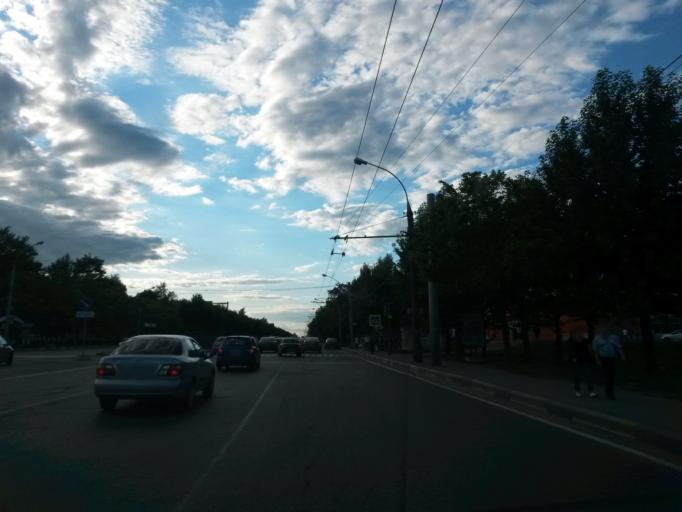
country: RU
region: Jaroslavl
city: Yaroslavl
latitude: 57.6858
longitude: 39.7850
